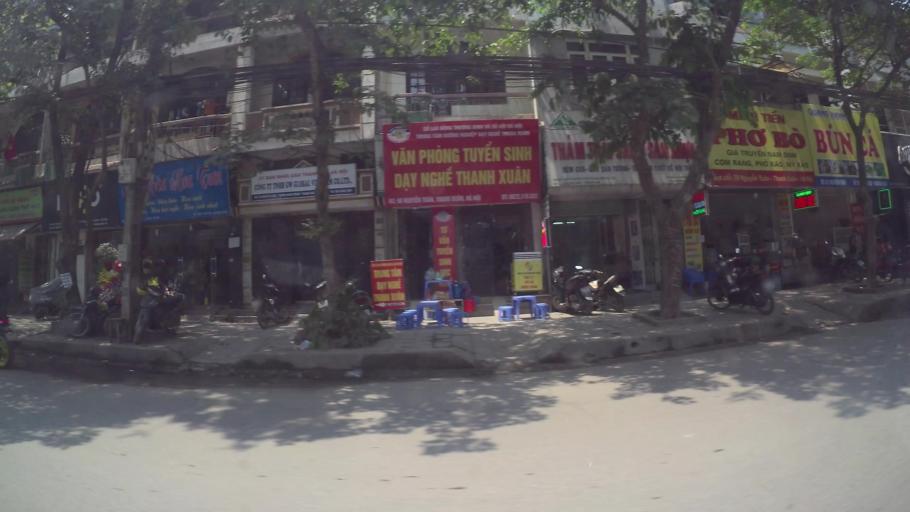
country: VN
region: Ha Noi
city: Thanh Xuan
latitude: 20.9959
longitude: 105.8054
